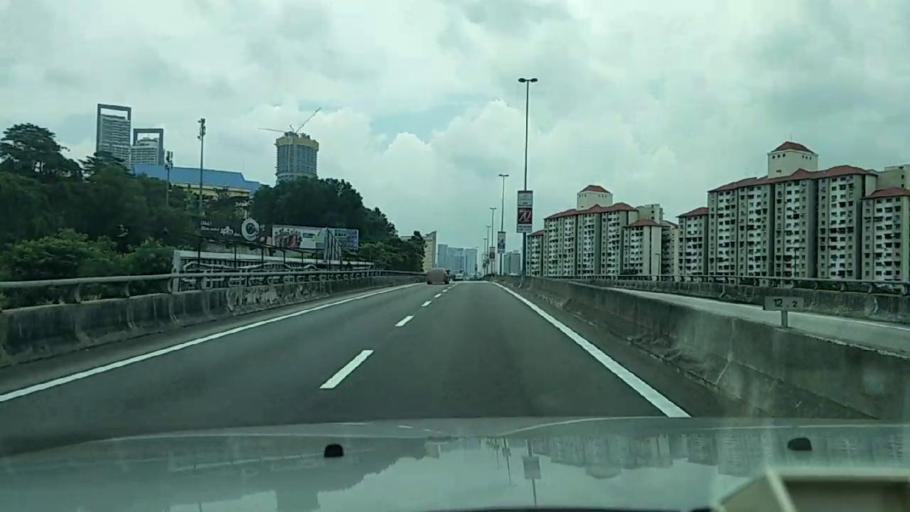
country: MY
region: Kuala Lumpur
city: Kuala Lumpur
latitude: 3.1066
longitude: 101.6729
